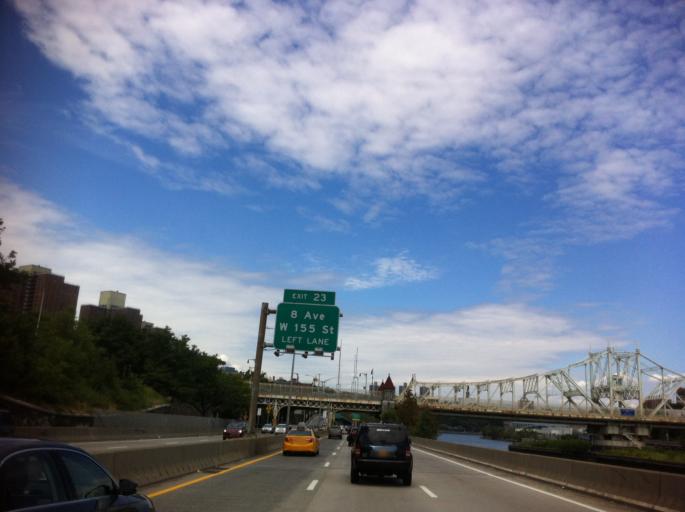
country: US
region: New Jersey
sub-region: Bergen County
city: Edgewater
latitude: 40.8240
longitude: -73.9344
